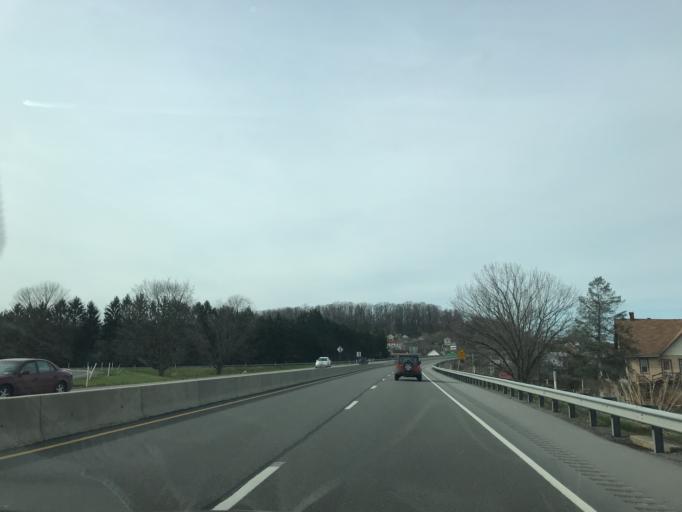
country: US
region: Pennsylvania
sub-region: Northumberland County
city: Milton
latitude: 41.0157
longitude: -76.8682
